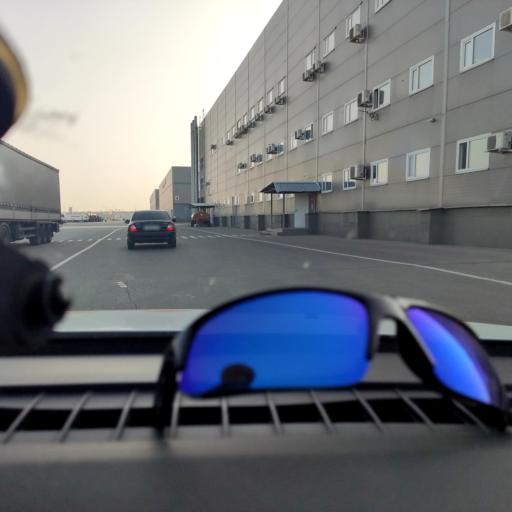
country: RU
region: Samara
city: Samara
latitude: 53.0971
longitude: 50.1338
